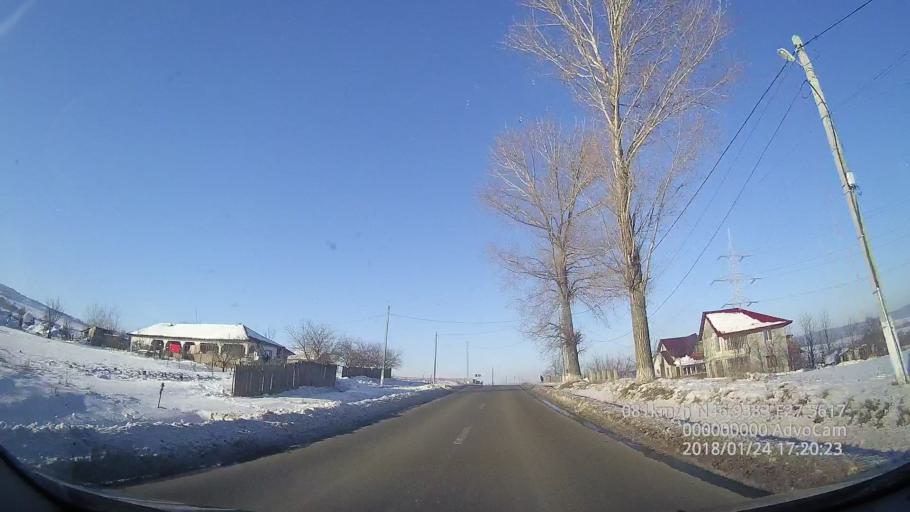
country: RO
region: Iasi
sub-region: Comuna Scanteia
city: Scanteia
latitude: 46.9388
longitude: 27.5615
